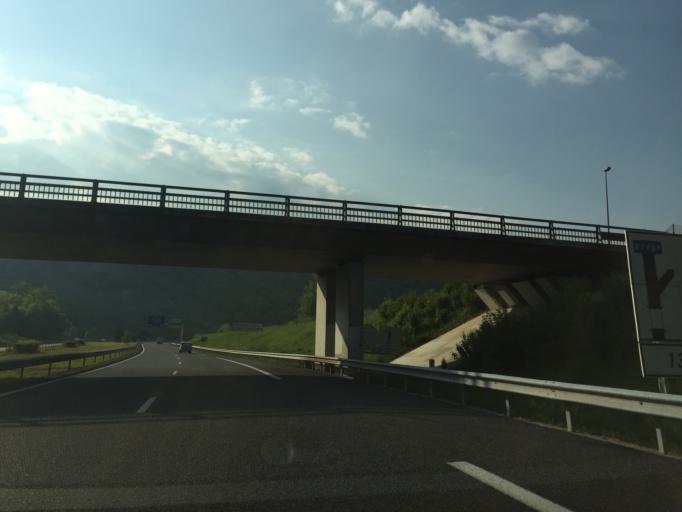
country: FR
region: Rhone-Alpes
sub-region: Departement de l'Isere
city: Allieres-et-Risset
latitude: 45.0868
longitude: 5.6710
